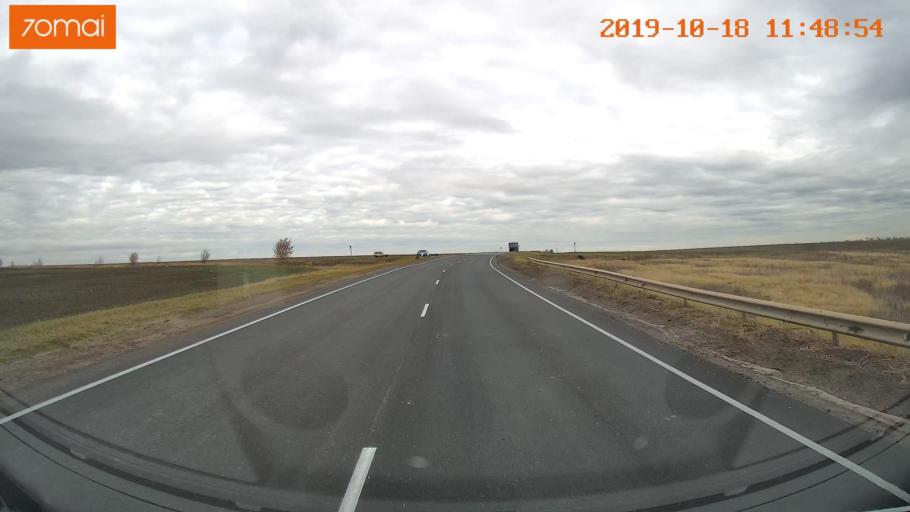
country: RU
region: Rjazan
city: Mikhaylov
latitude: 54.2442
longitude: 38.9856
